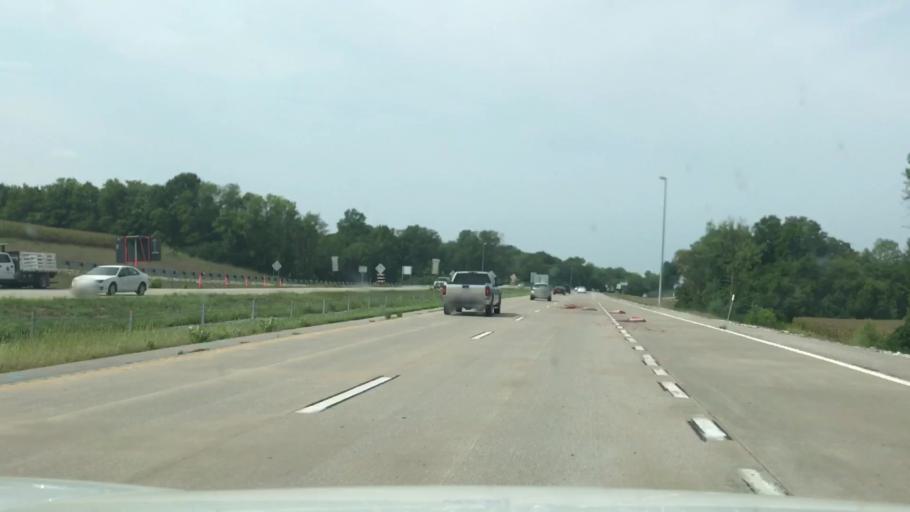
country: US
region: Missouri
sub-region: Saint Charles County
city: Cottleville
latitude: 38.7365
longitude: -90.6390
